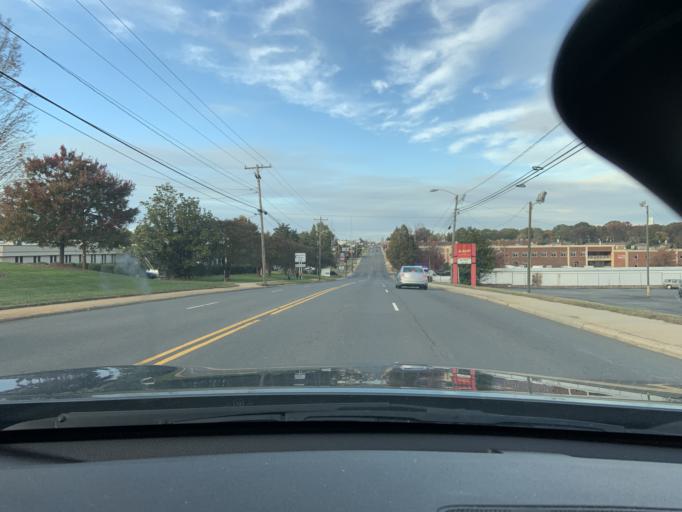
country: US
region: North Carolina
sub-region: Mecklenburg County
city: Charlotte
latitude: 35.1805
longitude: -80.8758
